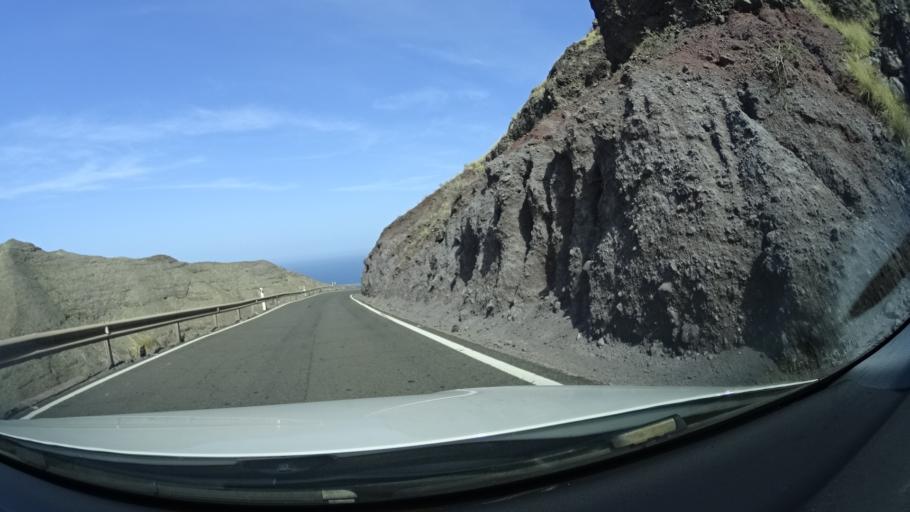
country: ES
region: Canary Islands
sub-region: Provincia de Las Palmas
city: Agaete
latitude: 28.0457
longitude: -15.7348
